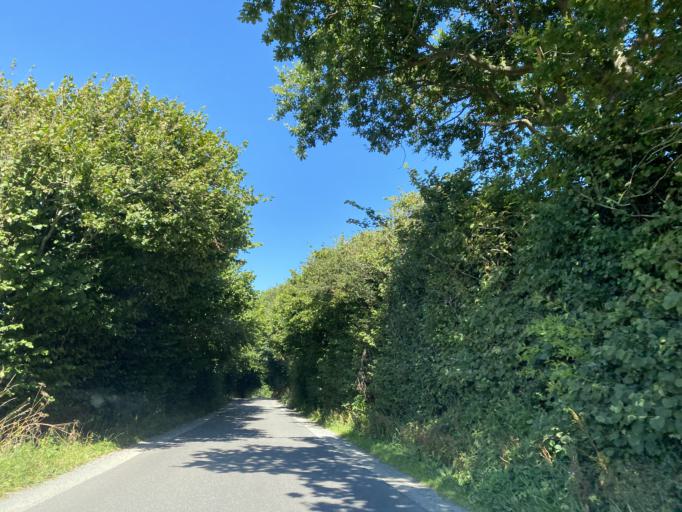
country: DK
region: South Denmark
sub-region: Kolding Kommune
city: Kolding
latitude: 55.5230
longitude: 9.5146
